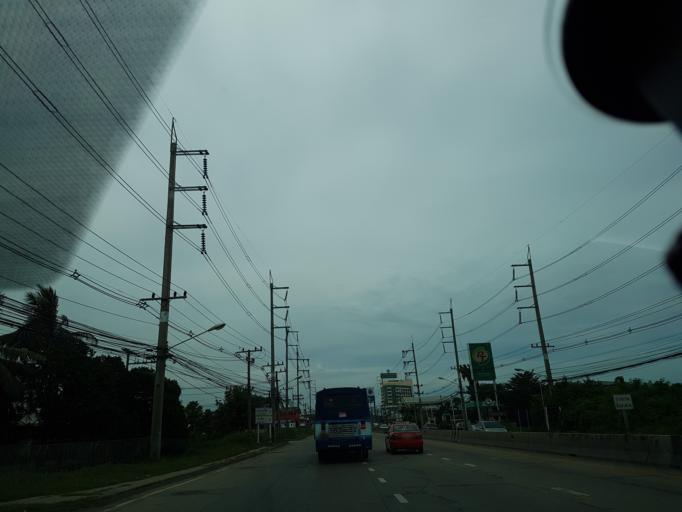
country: TH
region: Phra Nakhon Si Ayutthaya
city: Ban Bang Kadi Pathum Thani
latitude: 14.0104
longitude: 100.5537
